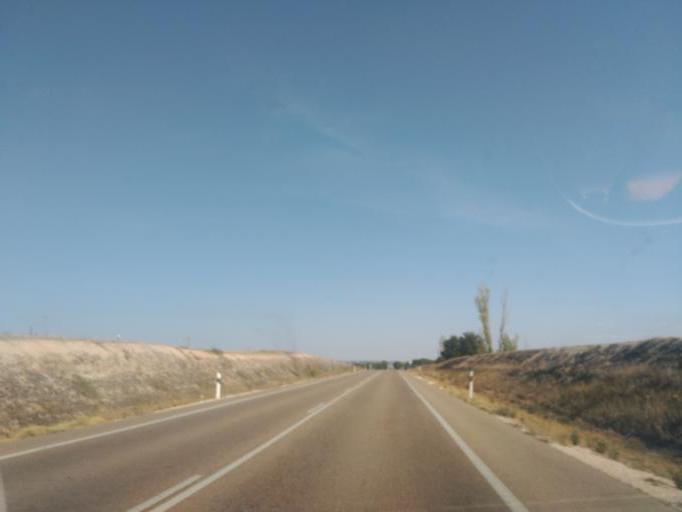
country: ES
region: Castille and Leon
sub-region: Provincia de Valladolid
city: Quintanilla de Arriba
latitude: 41.6155
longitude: -4.1914
